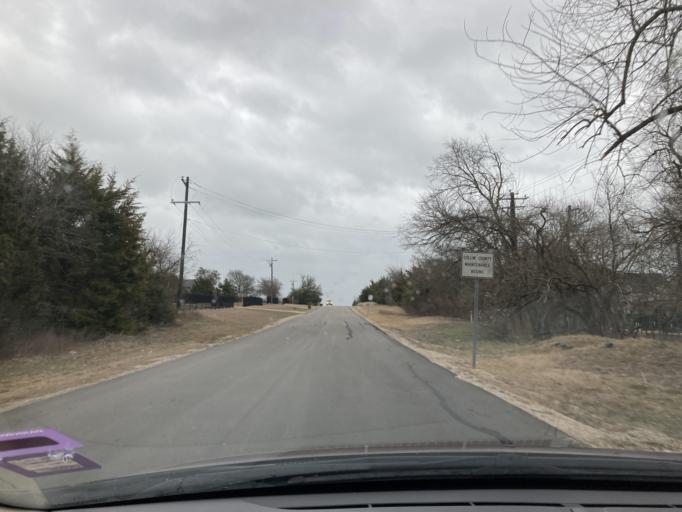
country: US
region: Texas
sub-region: Collin County
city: Lucas
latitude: 33.0806
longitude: -96.5603
